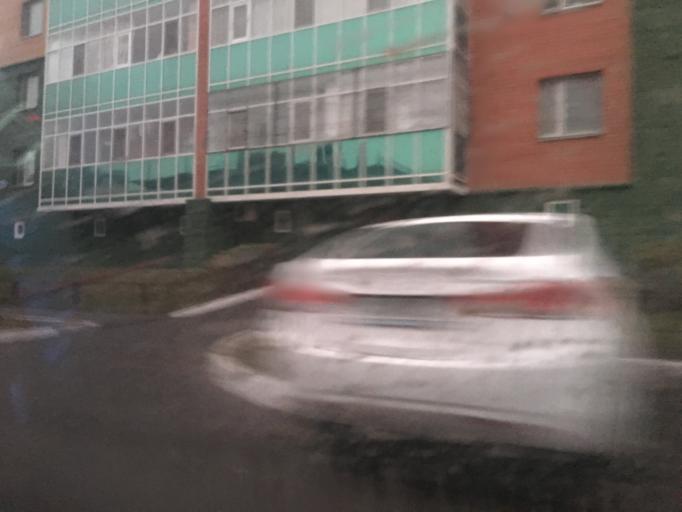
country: KZ
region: Astana Qalasy
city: Astana
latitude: 51.1601
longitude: 71.4359
